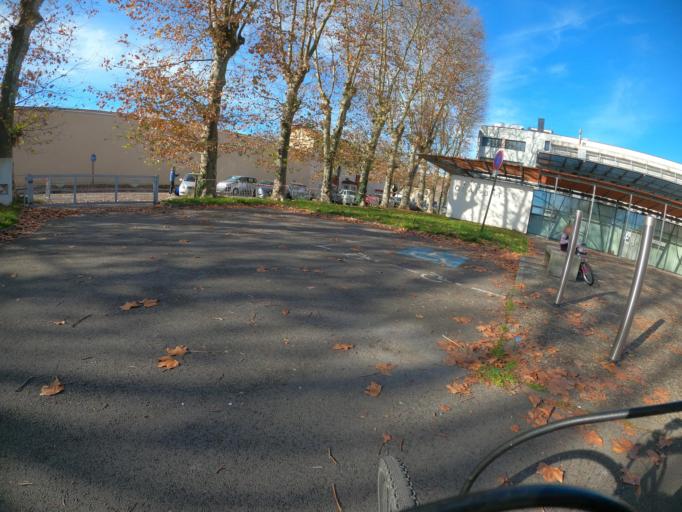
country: FR
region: Aquitaine
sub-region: Departement des Pyrenees-Atlantiques
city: Bayonne
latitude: 43.4917
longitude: -1.4627
